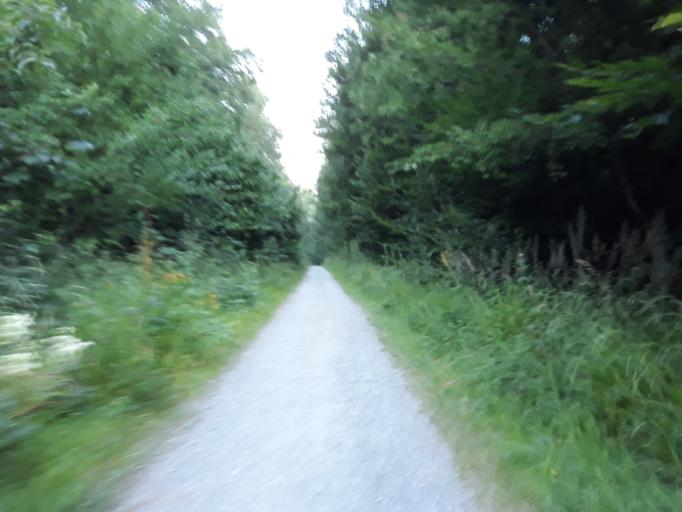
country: DE
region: Baden-Wuerttemberg
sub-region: Regierungsbezirk Stuttgart
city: Schonaich
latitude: 48.6708
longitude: 9.0520
